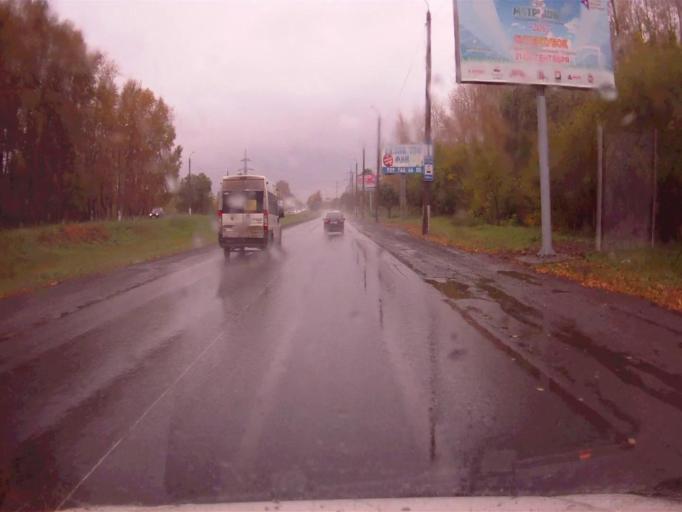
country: RU
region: Chelyabinsk
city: Dolgoderevenskoye
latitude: 55.2444
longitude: 61.3599
